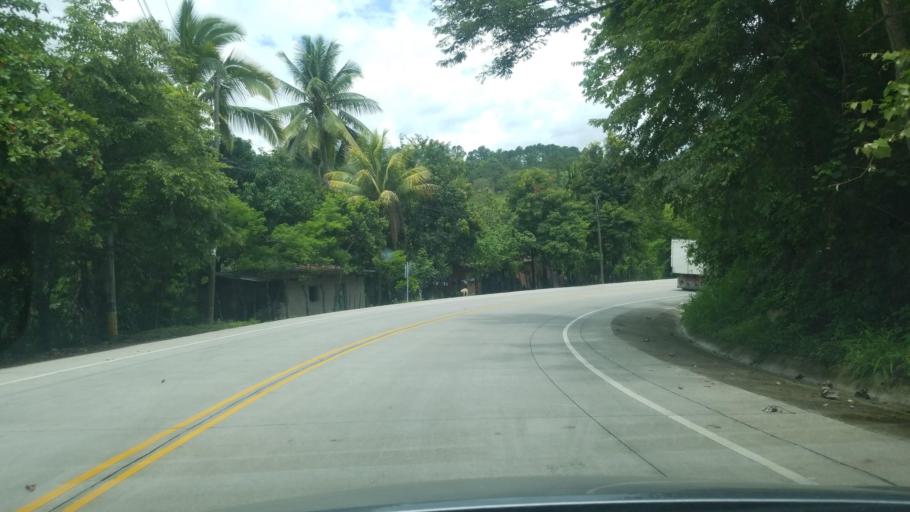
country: HN
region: Copan
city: Florida
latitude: 15.0232
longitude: -88.8317
